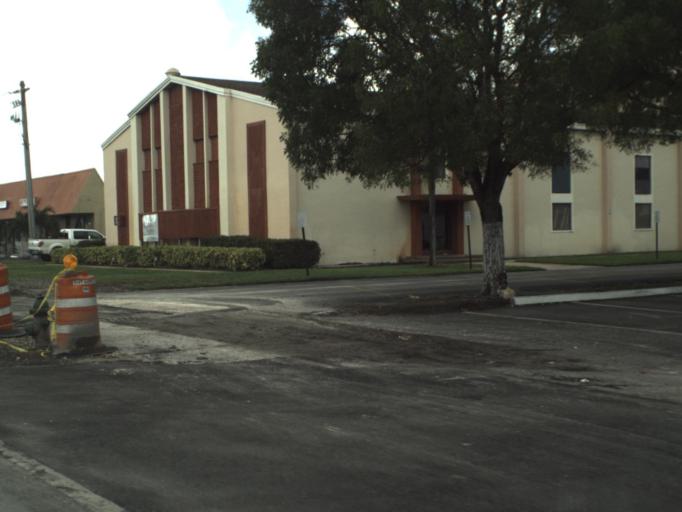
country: US
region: Florida
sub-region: Broward County
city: Pembroke Pines
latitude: 26.0260
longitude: -80.2083
